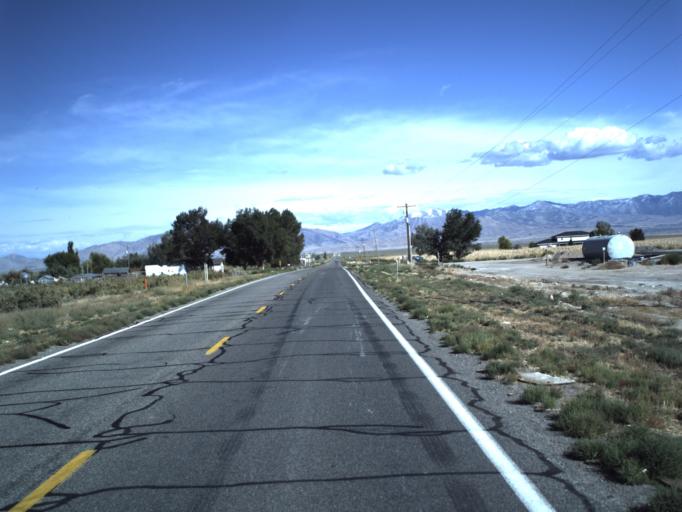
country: US
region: Utah
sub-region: Millard County
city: Delta
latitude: 39.3527
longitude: -112.5454
